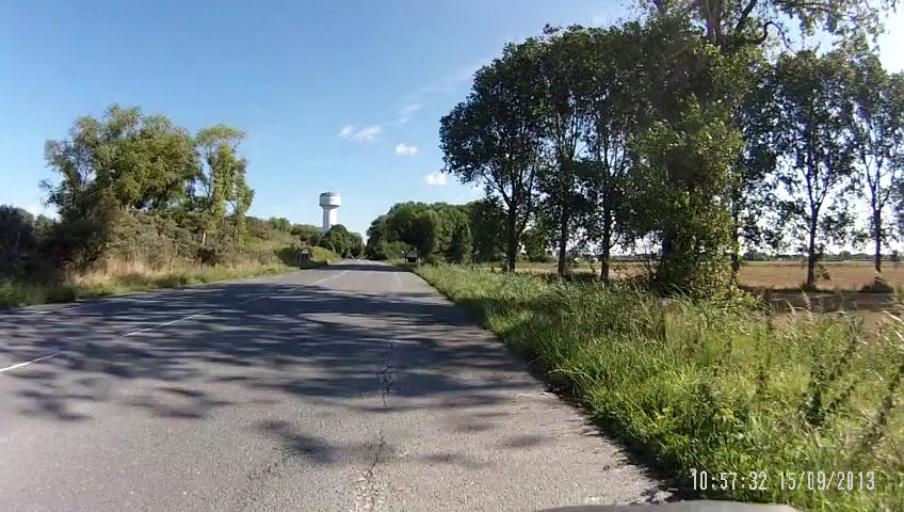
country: FR
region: Nord-Pas-de-Calais
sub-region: Departement du Nord
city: Zuydcoote
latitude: 51.0600
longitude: 2.4813
